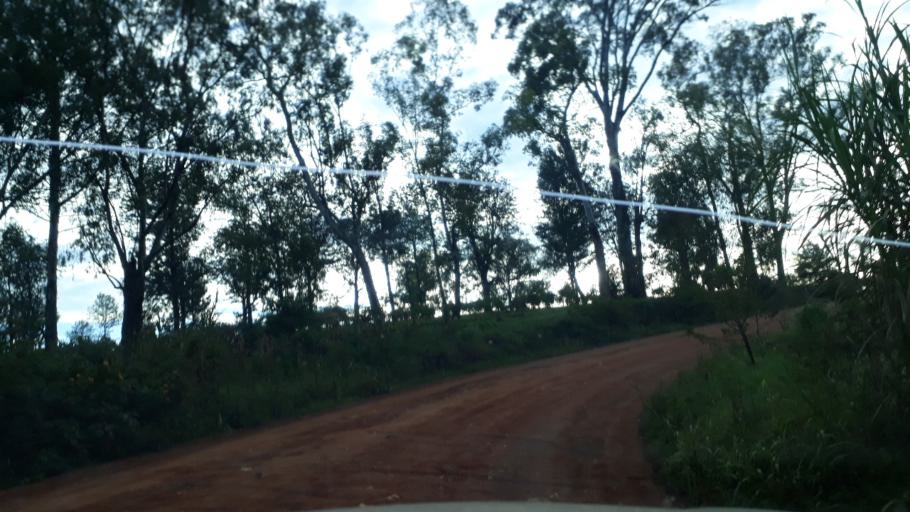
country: UG
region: Northern Region
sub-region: Zombo District
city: Paidha
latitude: 2.2300
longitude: 30.8240
